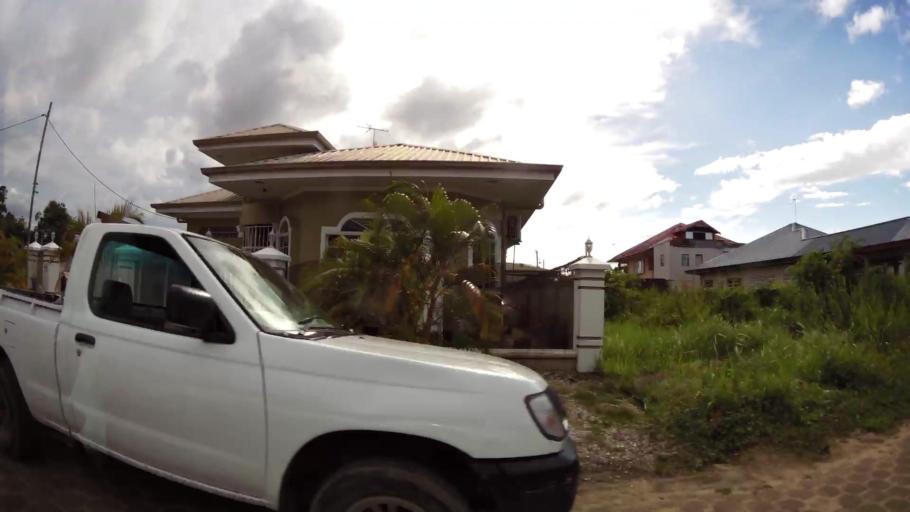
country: SR
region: Paramaribo
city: Paramaribo
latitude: 5.8548
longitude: -55.1776
